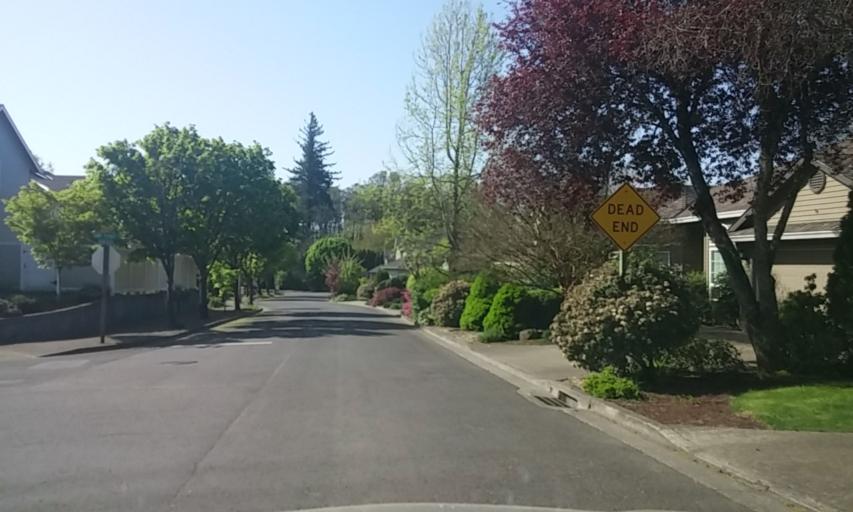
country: US
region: Oregon
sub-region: Washington County
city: Metzger
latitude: 45.4323
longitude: -122.7382
